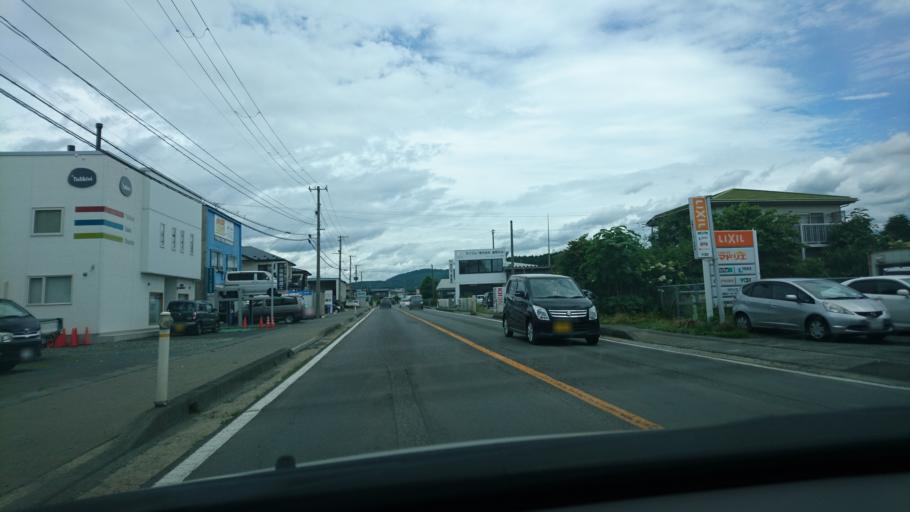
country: JP
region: Iwate
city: Morioka-shi
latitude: 39.6272
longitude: 141.1832
